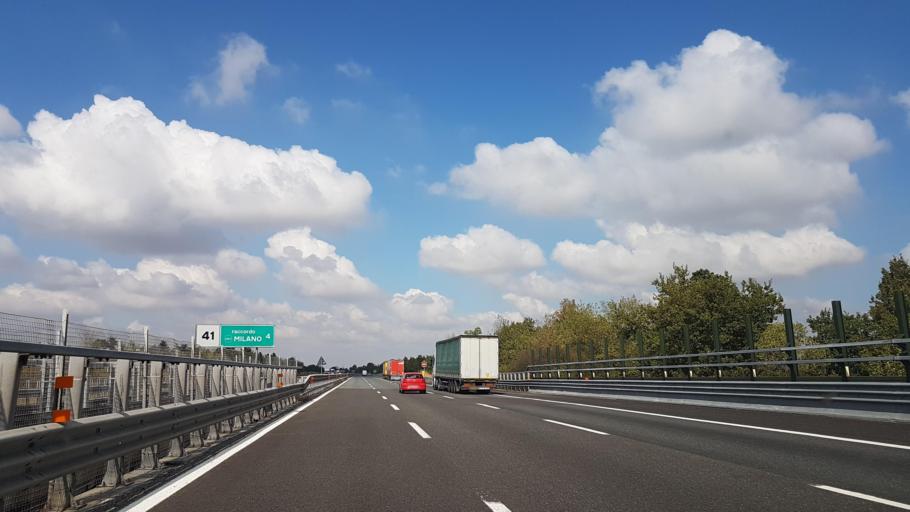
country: IT
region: Piedmont
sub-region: Provincia di Alessandria
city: Capriata d'Orba
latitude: 44.7264
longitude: 8.6660
